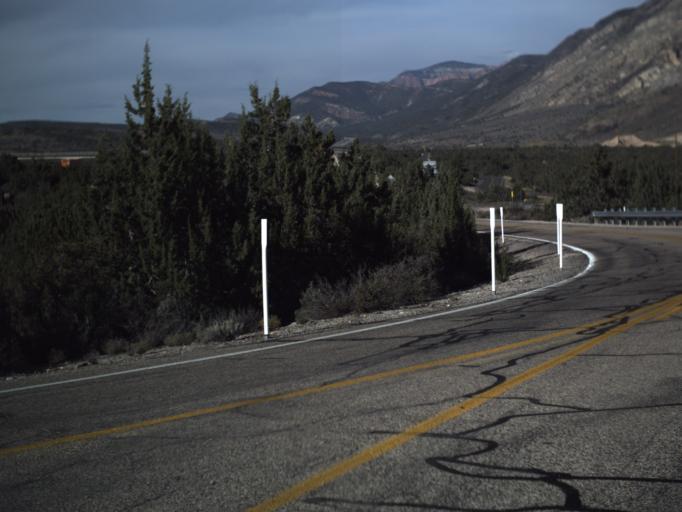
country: US
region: Utah
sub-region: Washington County
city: Toquerville
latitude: 37.3218
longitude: -113.2870
